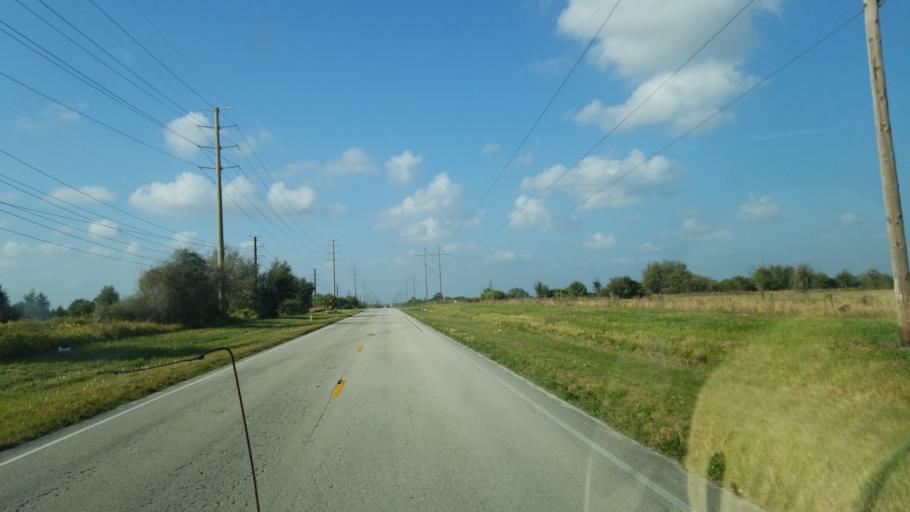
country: US
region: Florida
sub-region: Hardee County
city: Wauchula
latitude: 27.5501
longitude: -81.9316
